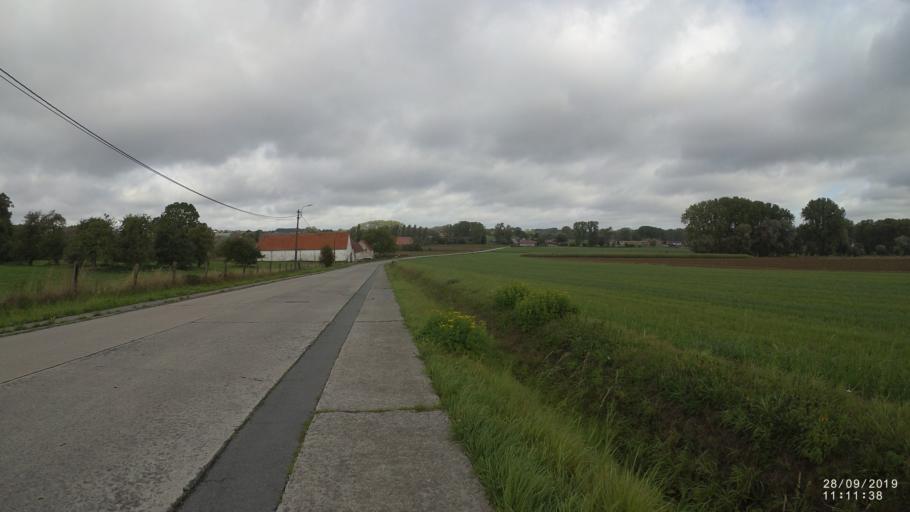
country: BE
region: Flanders
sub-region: Provincie Oost-Vlaanderen
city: Sint-Maria-Lierde
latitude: 50.8185
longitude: 3.8226
